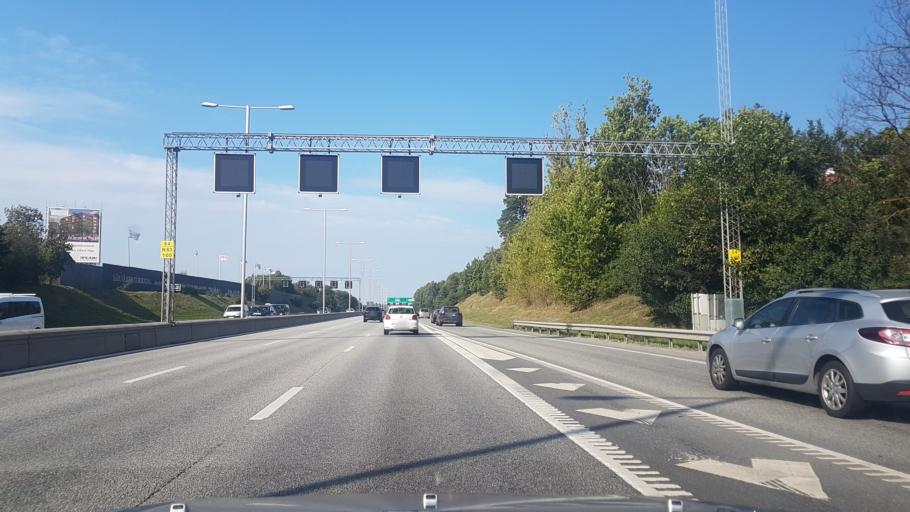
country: SE
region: Stockholm
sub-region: Solna Kommun
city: Solna
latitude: 59.3811
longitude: 18.0099
